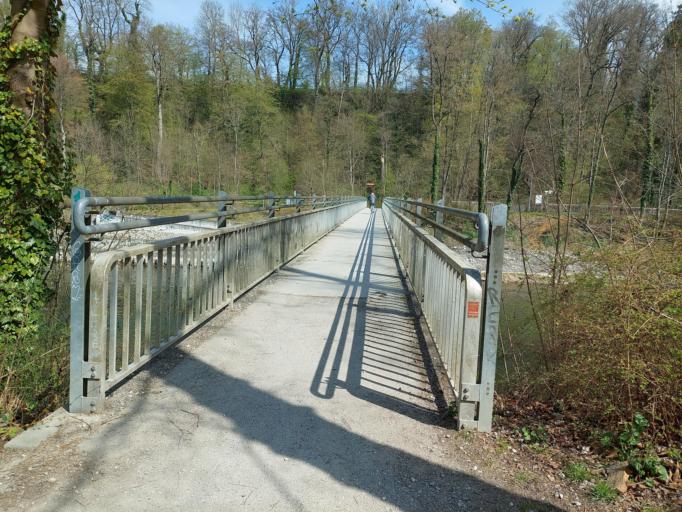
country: DE
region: Bavaria
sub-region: Upper Bavaria
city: Dachau
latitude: 48.2561
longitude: 11.4276
